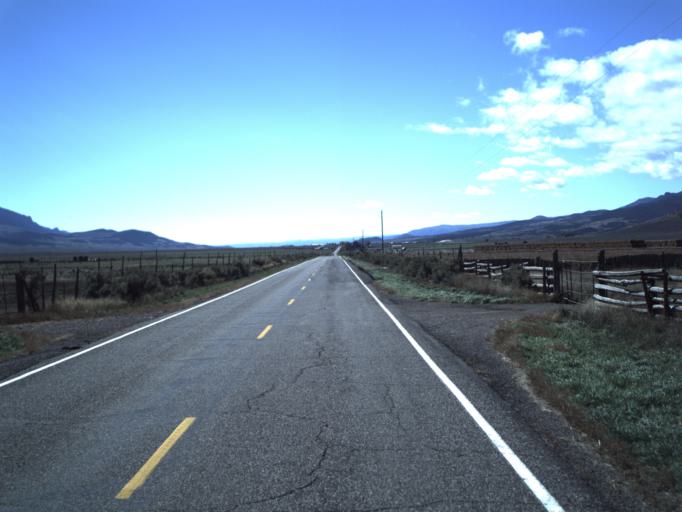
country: US
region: Utah
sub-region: Sevier County
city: Monroe
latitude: 38.4692
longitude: -111.9059
